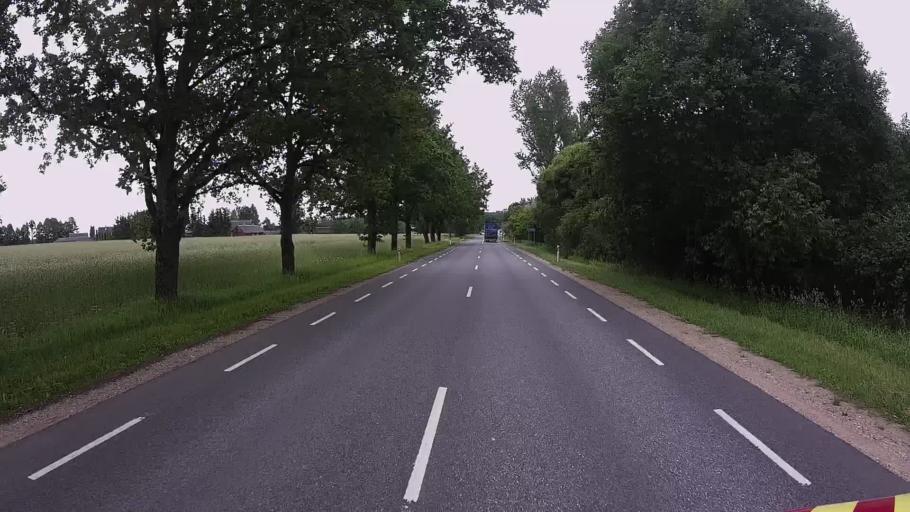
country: EE
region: Viljandimaa
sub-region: Karksi vald
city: Karksi-Nuia
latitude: 58.1231
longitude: 25.5825
